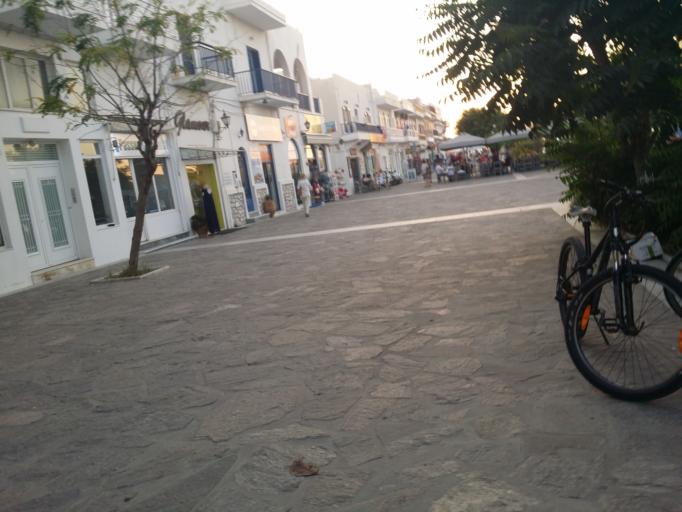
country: GR
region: South Aegean
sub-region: Nomos Kykladon
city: Paros
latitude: 37.0851
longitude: 25.1513
